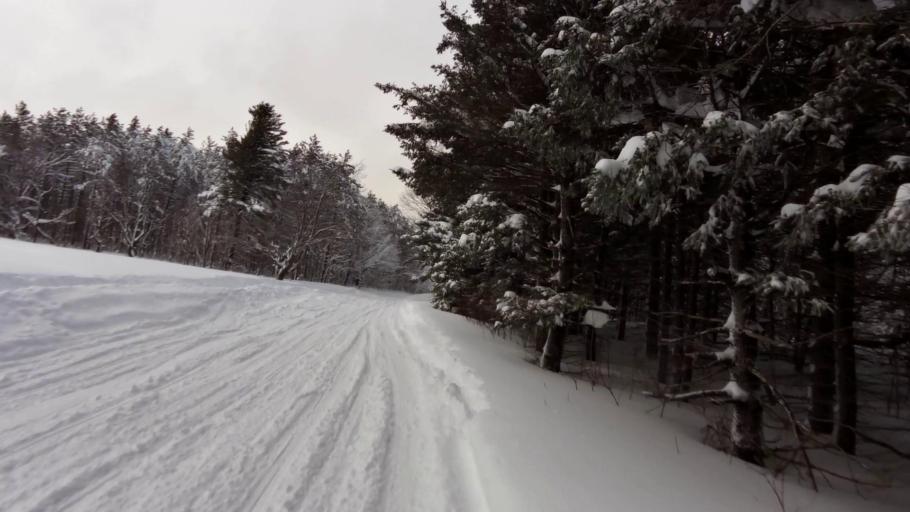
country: US
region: New York
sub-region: Lewis County
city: Lowville
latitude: 43.7444
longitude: -75.6743
